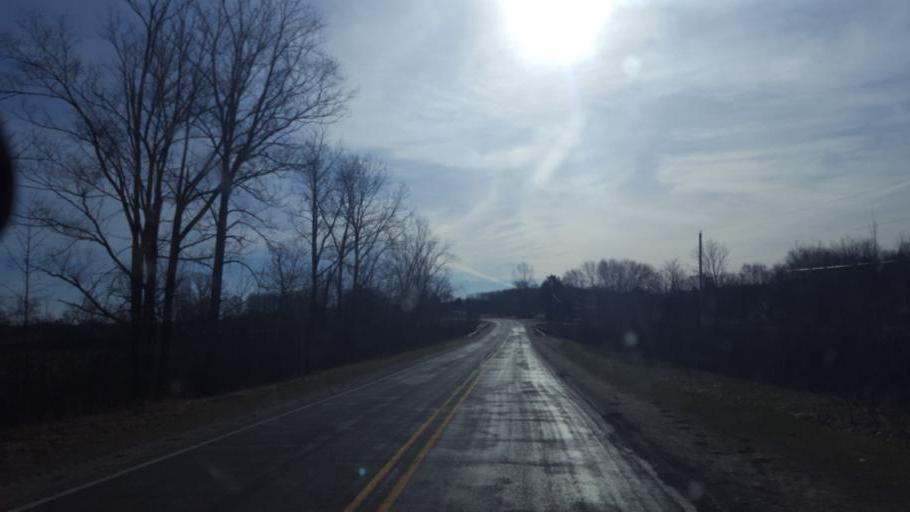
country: US
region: Michigan
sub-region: Montcalm County
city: Howard City
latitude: 43.4907
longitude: -85.4334
